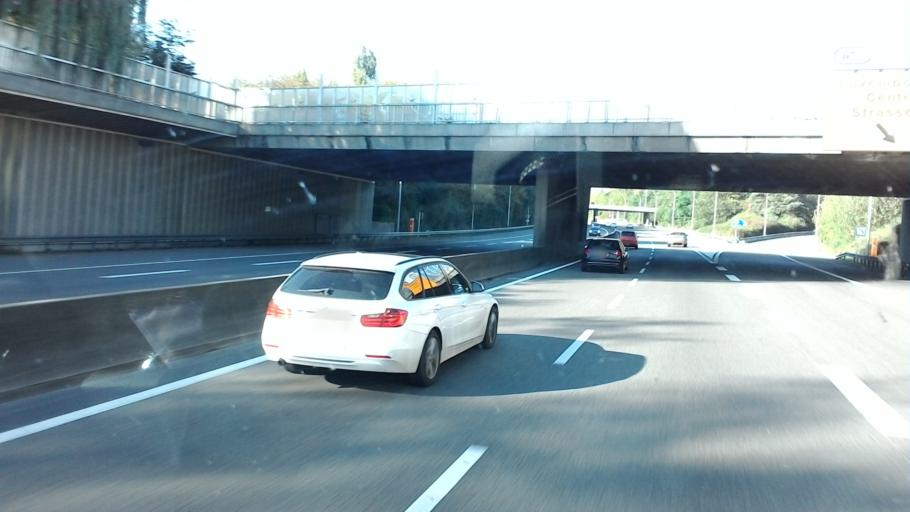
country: LU
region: Luxembourg
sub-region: Canton de Luxembourg
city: Strassen
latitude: 49.6181
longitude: 6.0835
